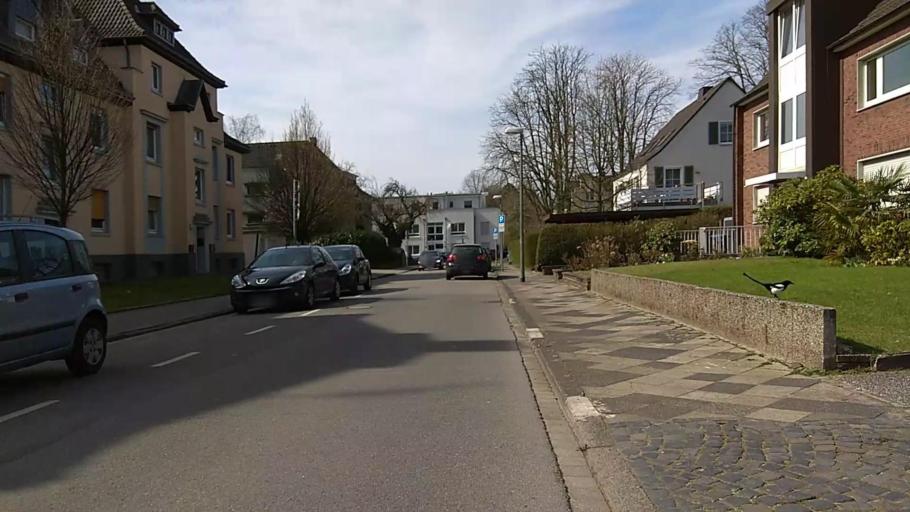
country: DE
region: North Rhine-Westphalia
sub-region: Regierungsbezirk Munster
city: Gladbeck
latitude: 51.5771
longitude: 7.0624
